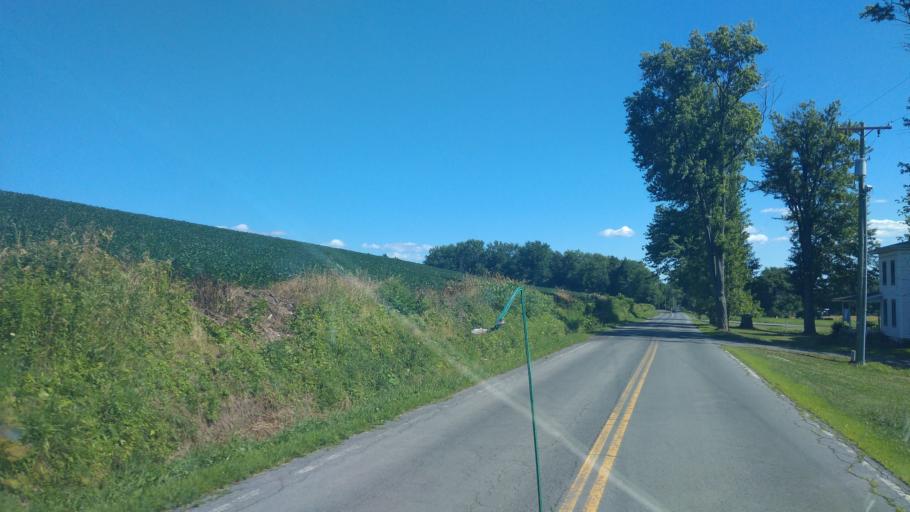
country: US
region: New York
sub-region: Wayne County
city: Clyde
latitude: 43.0150
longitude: -76.8118
